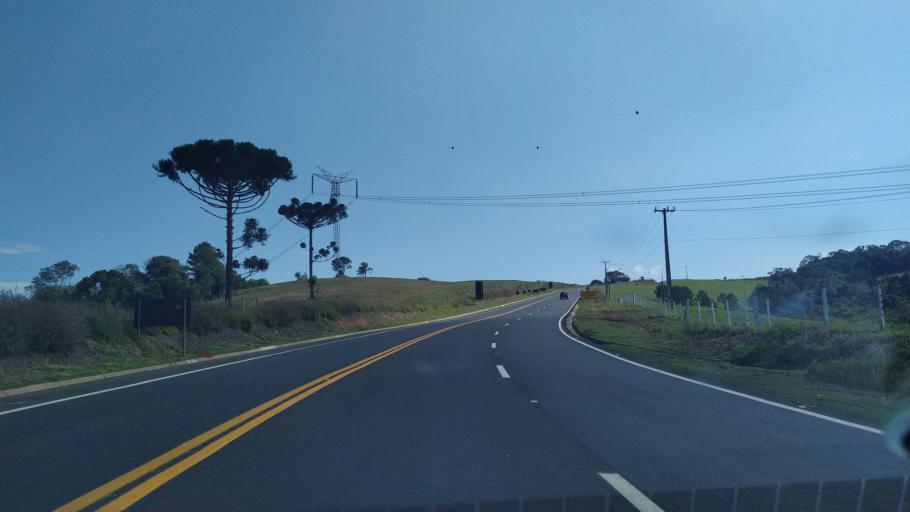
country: BR
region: Parana
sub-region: Telemaco Borba
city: Telemaco Borba
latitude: -24.2858
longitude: -50.7089
